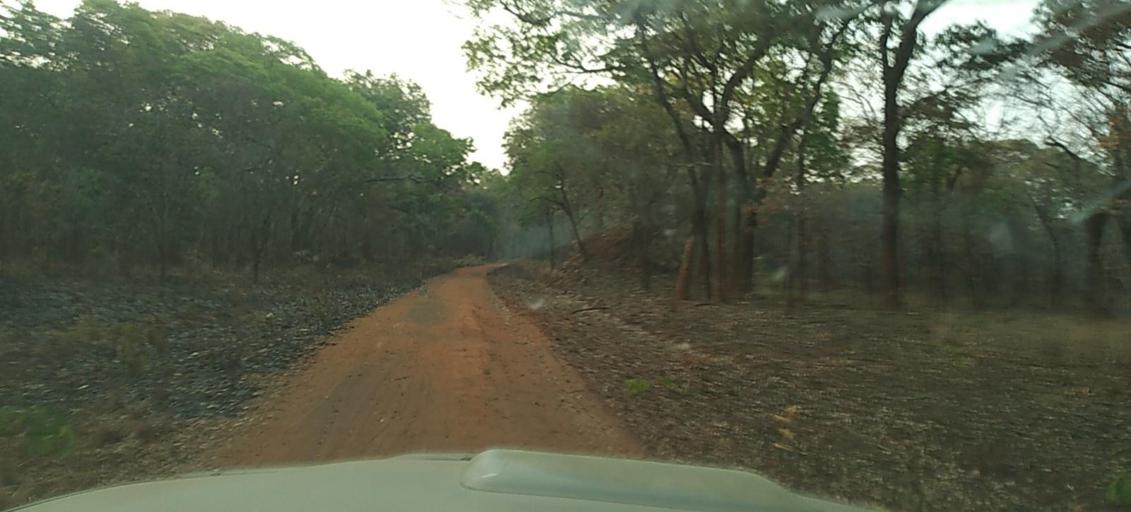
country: ZM
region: North-Western
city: Kasempa
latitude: -13.1104
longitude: 26.4055
